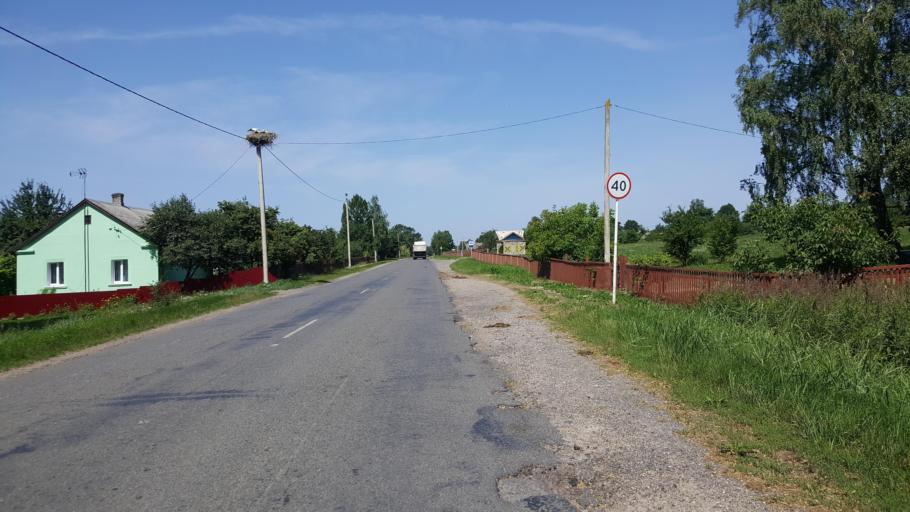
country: BY
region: Brest
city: Vysokaye
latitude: 52.3596
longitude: 23.5356
